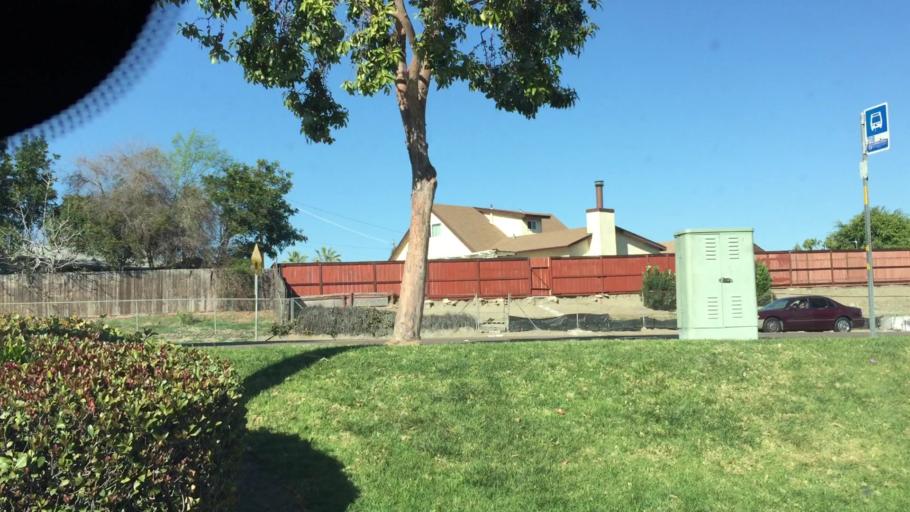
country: US
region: California
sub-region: San Diego County
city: Vista
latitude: 33.2211
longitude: -117.2435
